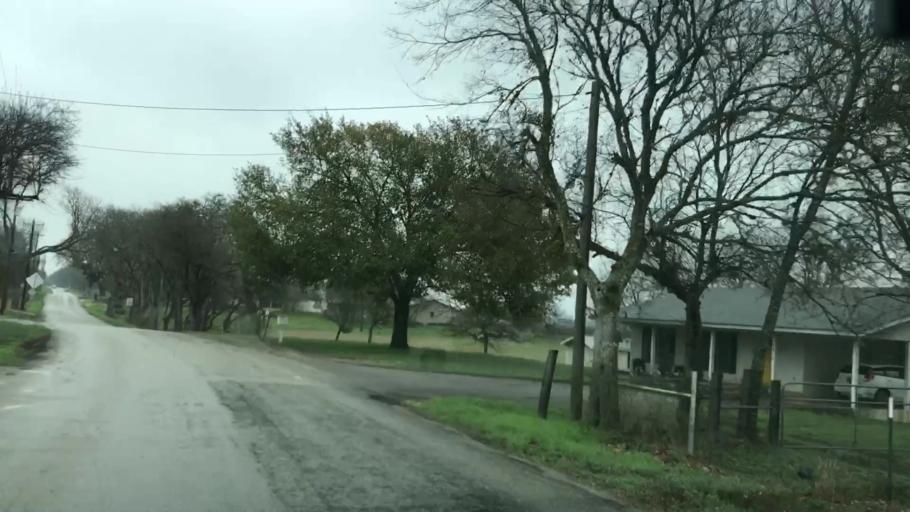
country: US
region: Texas
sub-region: Hays County
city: San Marcos
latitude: 29.8944
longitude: -97.8974
